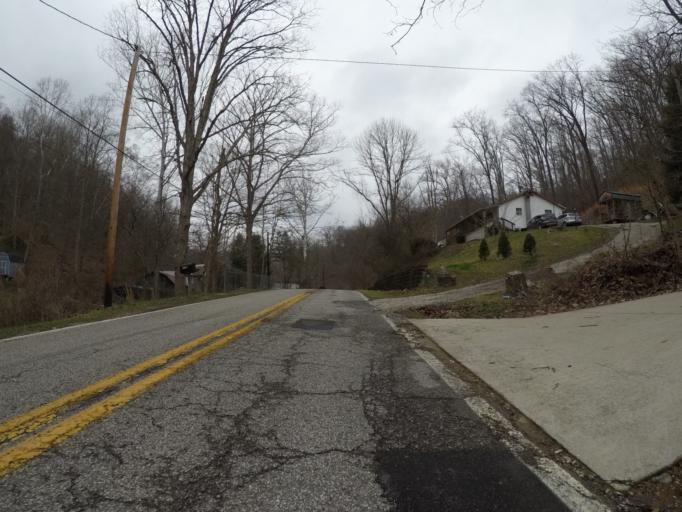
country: US
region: West Virginia
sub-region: Cabell County
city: Barboursville
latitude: 38.4489
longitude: -82.2576
